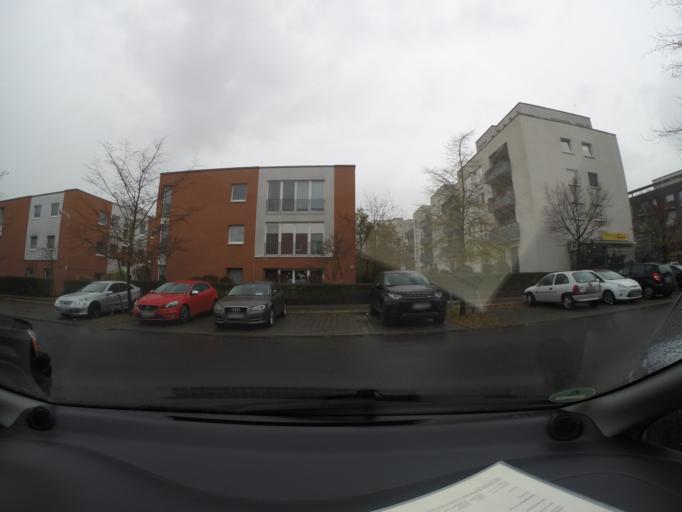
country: DE
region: Berlin
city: Neu-Hohenschoenhausen
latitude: 52.5473
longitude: 13.5291
